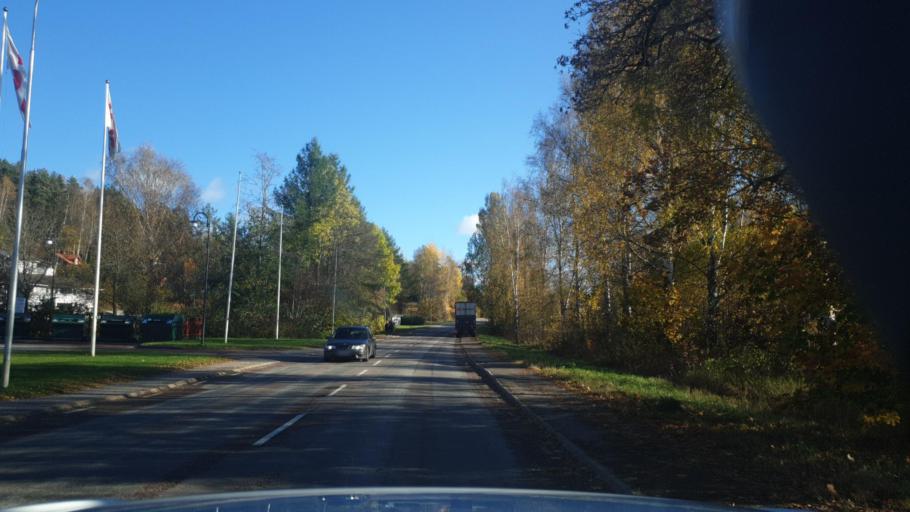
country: SE
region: Vaermland
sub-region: Arvika Kommun
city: Arvika
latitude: 59.6287
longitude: 12.8251
